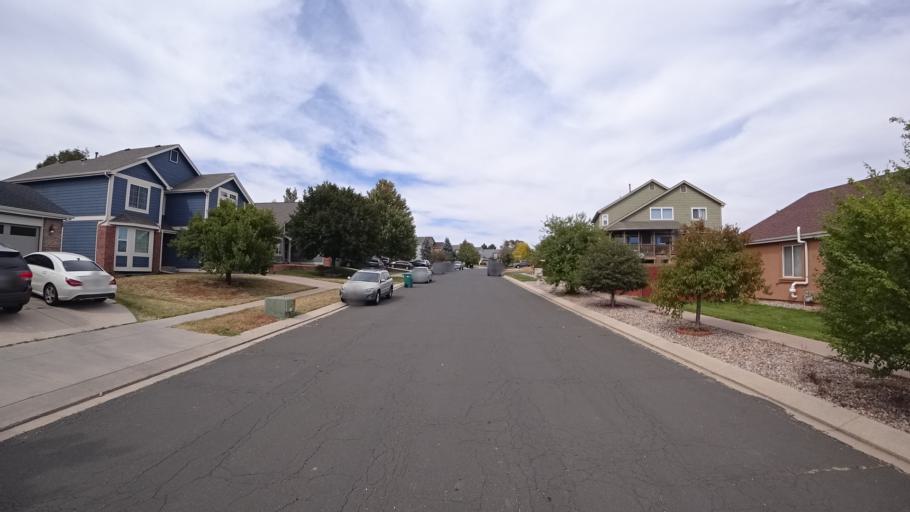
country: US
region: Colorado
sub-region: El Paso County
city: Cimarron Hills
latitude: 38.9000
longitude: -104.7090
